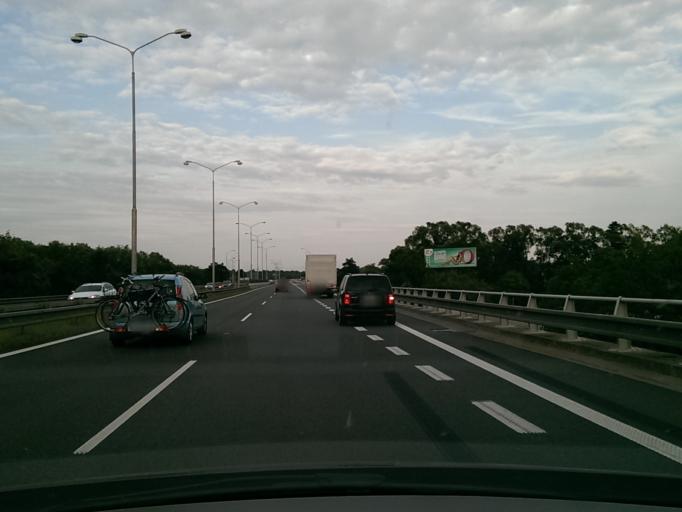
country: CZ
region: South Moravian
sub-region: Mesto Brno
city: Brno
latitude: 49.1592
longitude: 16.6227
